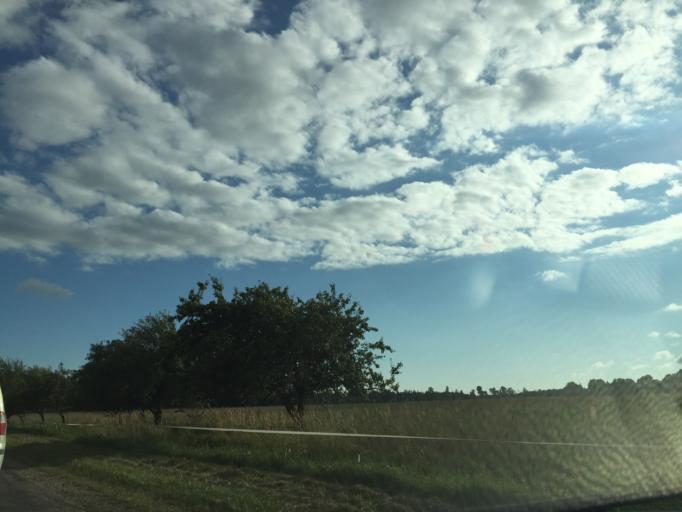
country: LV
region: Krimulda
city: Ragana
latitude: 57.3057
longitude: 24.6448
